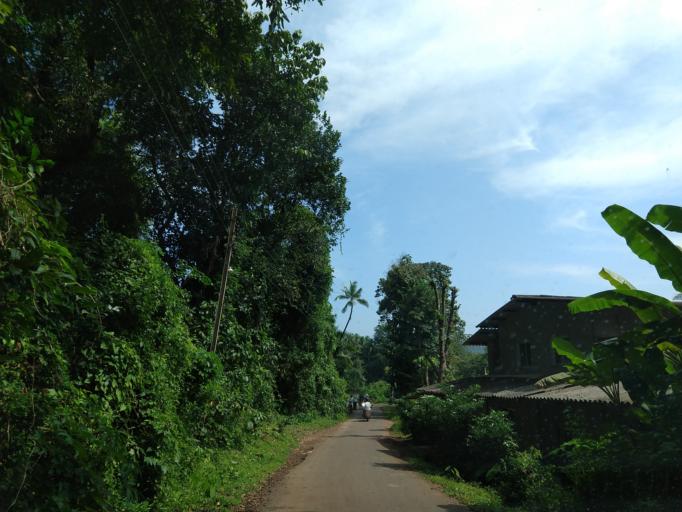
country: IN
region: Maharashtra
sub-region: Sindhudurg
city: Kudal
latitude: 16.0425
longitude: 73.6840
